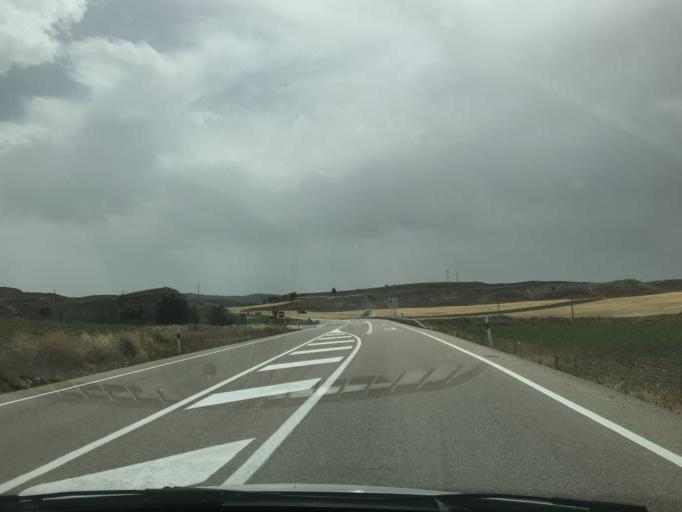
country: ES
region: Castille-La Mancha
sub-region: Provincia de Cuenca
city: Villar de Domingo Garcia
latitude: 40.2454
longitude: -2.3038
